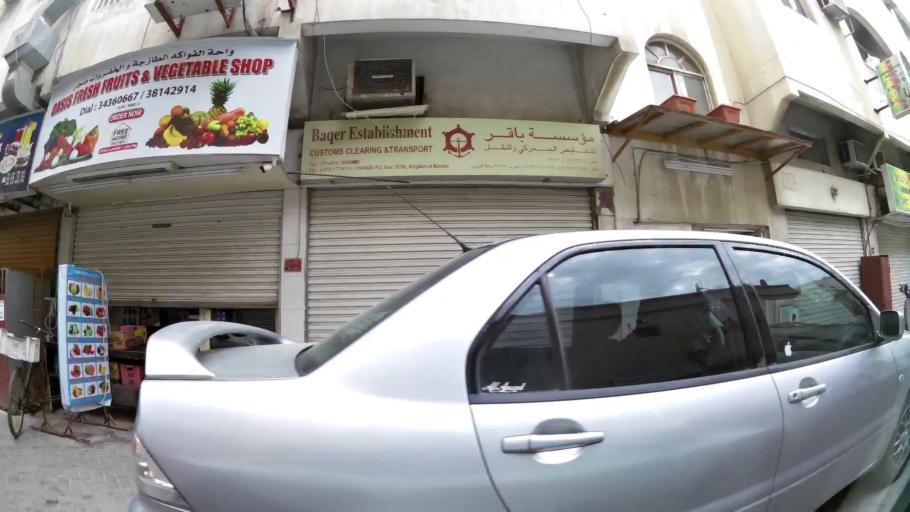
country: BH
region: Manama
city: Manama
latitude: 26.2256
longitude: 50.5924
